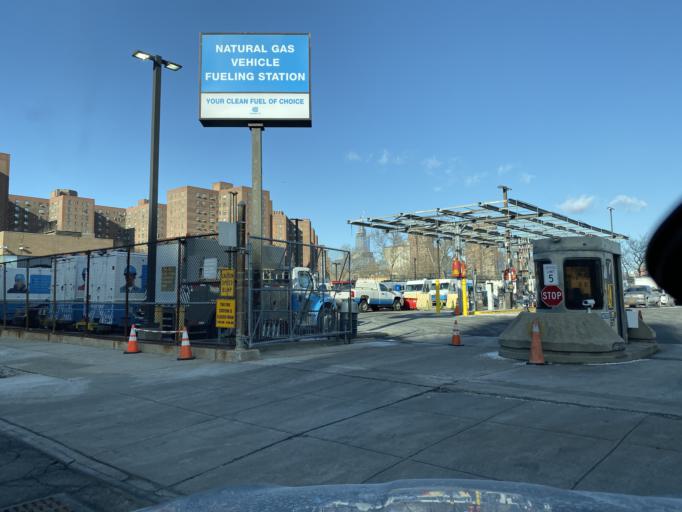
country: US
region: New York
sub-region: Queens County
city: Long Island City
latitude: 40.7293
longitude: -73.9734
